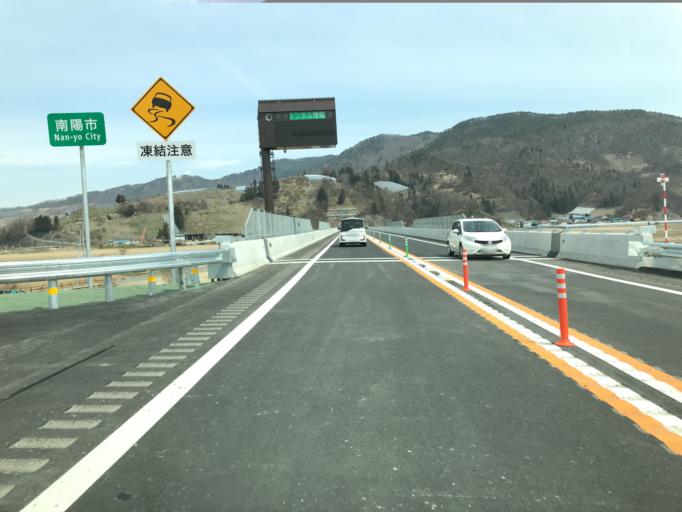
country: JP
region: Yamagata
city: Takahata
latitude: 38.0381
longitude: 140.1867
